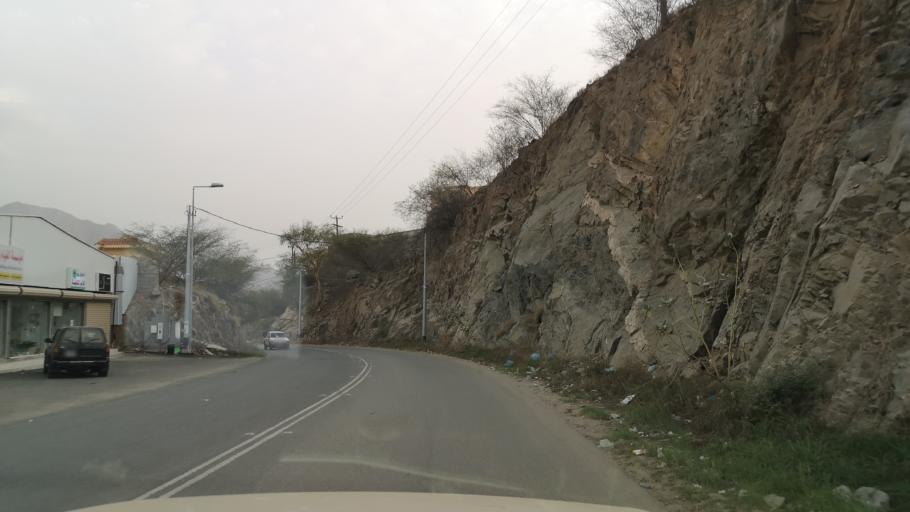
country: YE
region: Sa'dah
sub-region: Monabbih
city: Suq al Khamis
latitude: 17.3598
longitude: 43.1293
